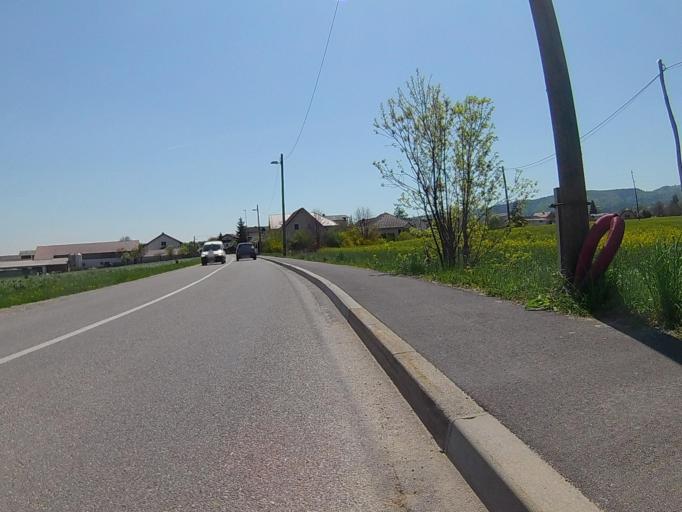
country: SI
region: Hoce-Slivnica
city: Spodnje Hoce
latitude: 46.5044
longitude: 15.6420
